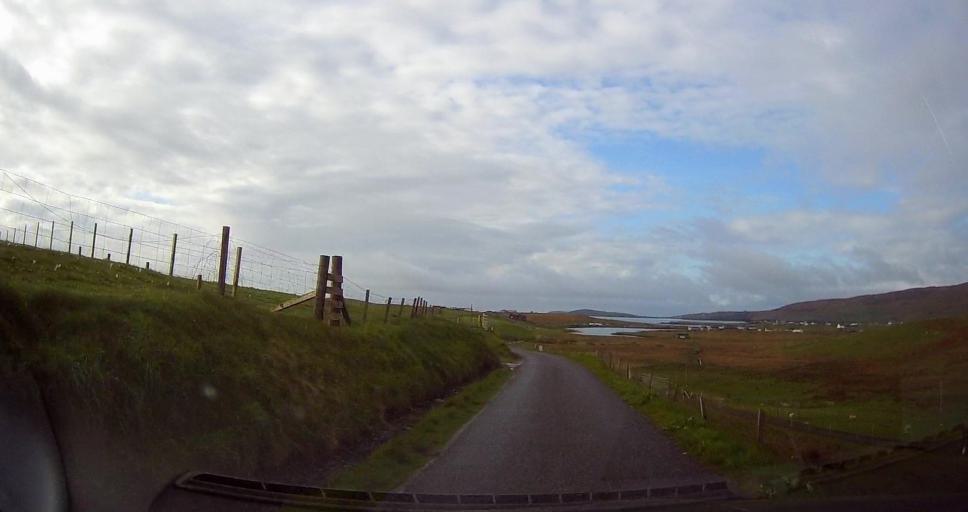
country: GB
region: Scotland
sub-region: Shetland Islands
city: Sandwick
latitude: 60.0529
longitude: -1.2076
